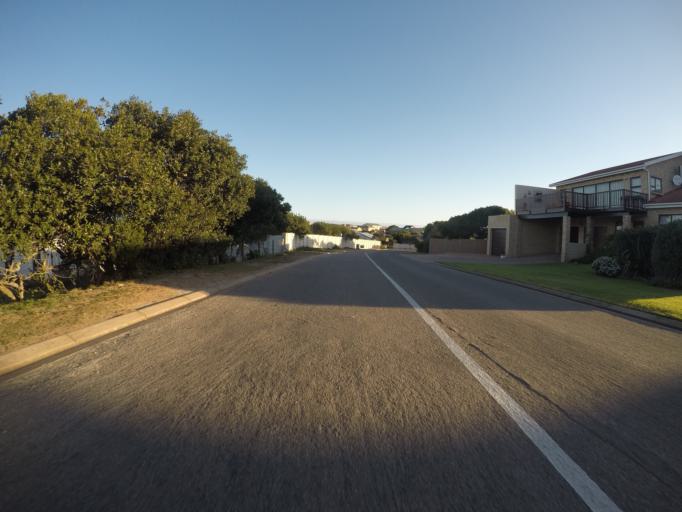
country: ZA
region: Western Cape
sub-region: Eden District Municipality
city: Riversdale
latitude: -34.3845
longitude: 21.4027
